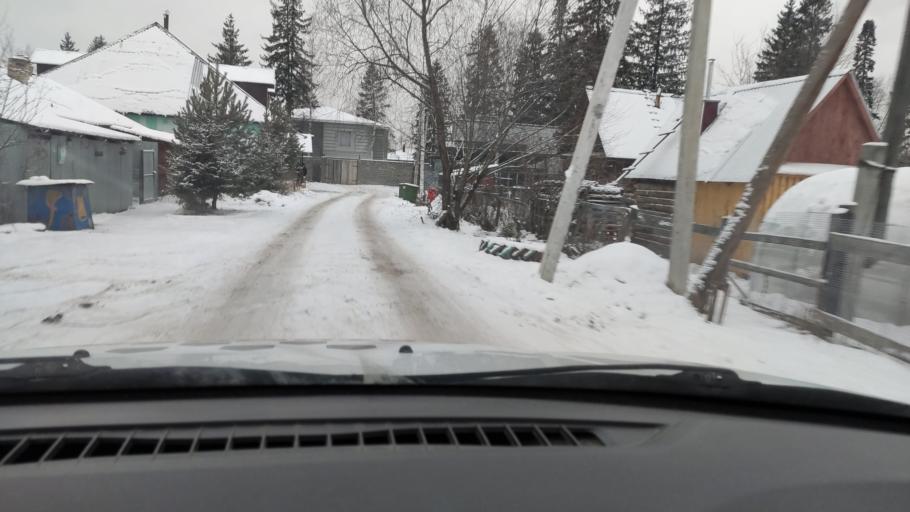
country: RU
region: Perm
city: Perm
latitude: 57.9941
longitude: 56.3355
